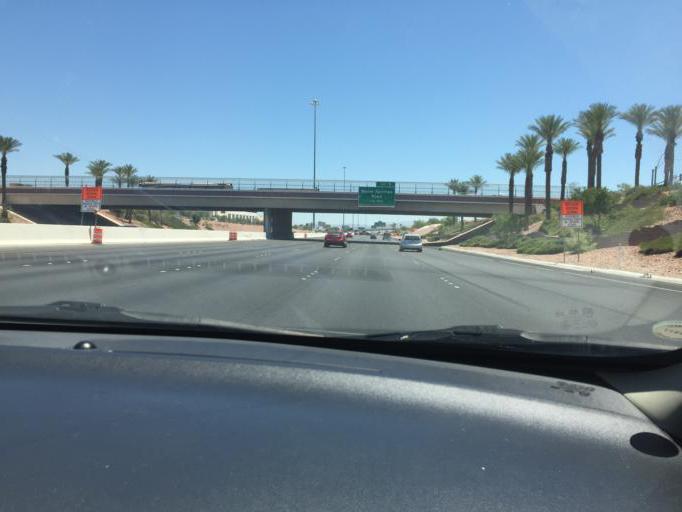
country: US
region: Nevada
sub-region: Clark County
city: Paradise
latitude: 36.0635
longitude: -115.1646
